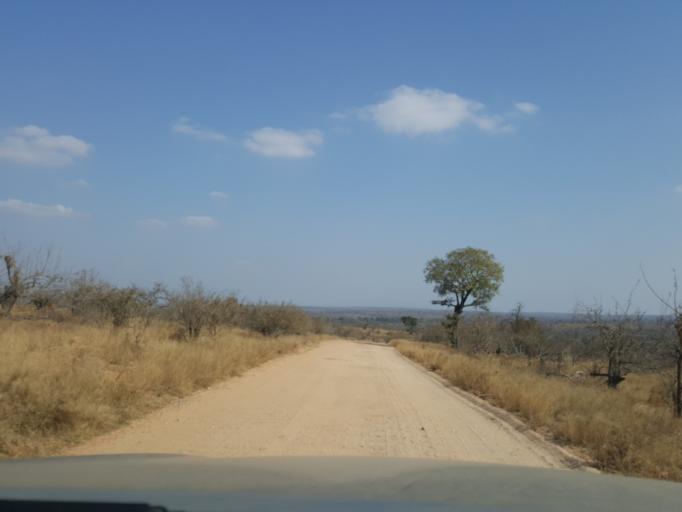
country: ZA
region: Mpumalanga
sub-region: Ehlanzeni District
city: Komatipoort
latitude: -25.3031
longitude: 31.7538
